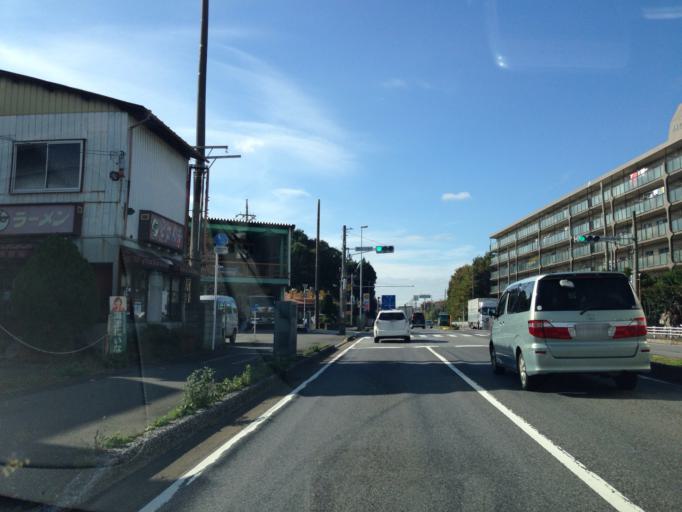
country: JP
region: Chiba
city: Abiko
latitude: 35.8775
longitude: 140.0045
